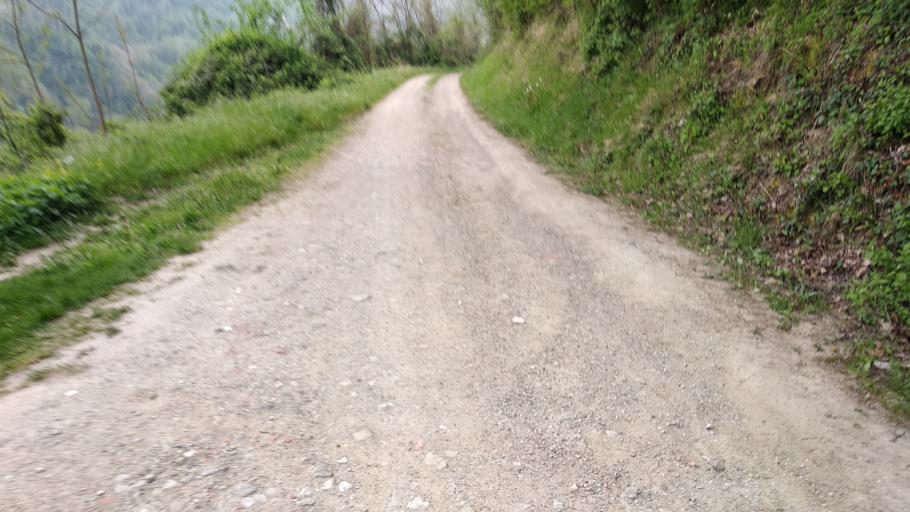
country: IT
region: Emilia-Romagna
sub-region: Forli-Cesena
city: Modigliana
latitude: 44.1491
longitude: 11.7972
